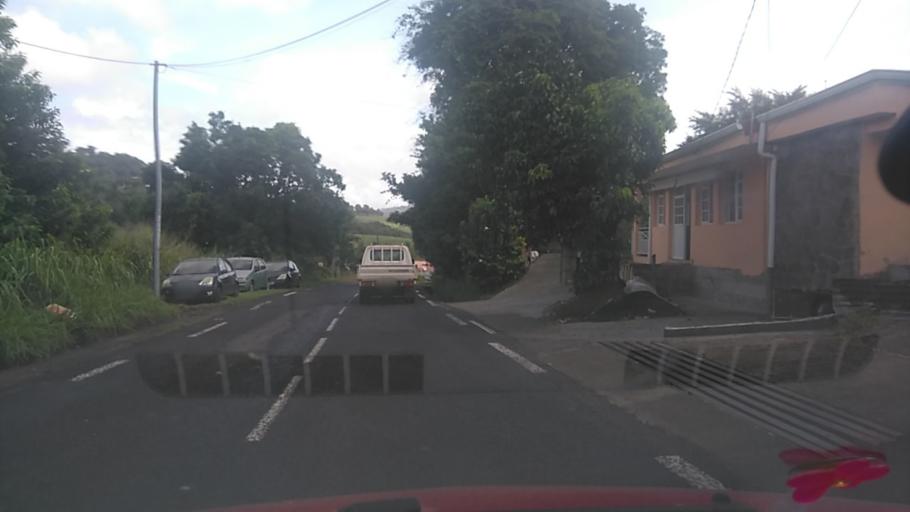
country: MQ
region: Martinique
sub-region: Martinique
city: Saint-Esprit
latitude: 14.5711
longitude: -60.9334
